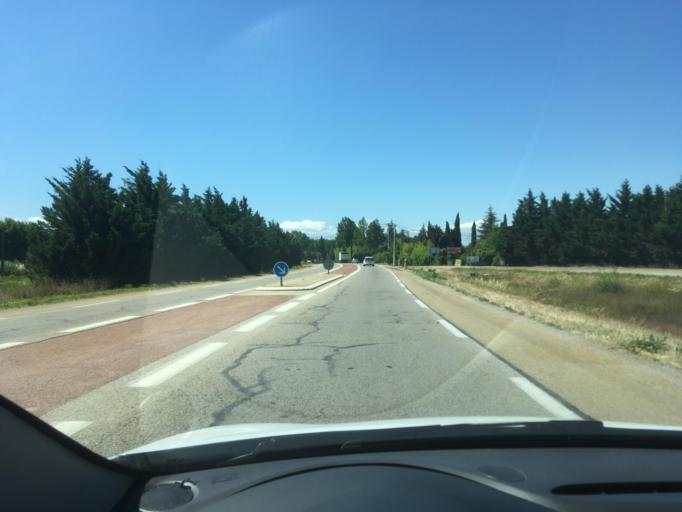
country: FR
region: Provence-Alpes-Cote d'Azur
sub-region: Departement des Bouches-du-Rhone
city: Chateaurenard
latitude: 43.8903
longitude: 4.8342
